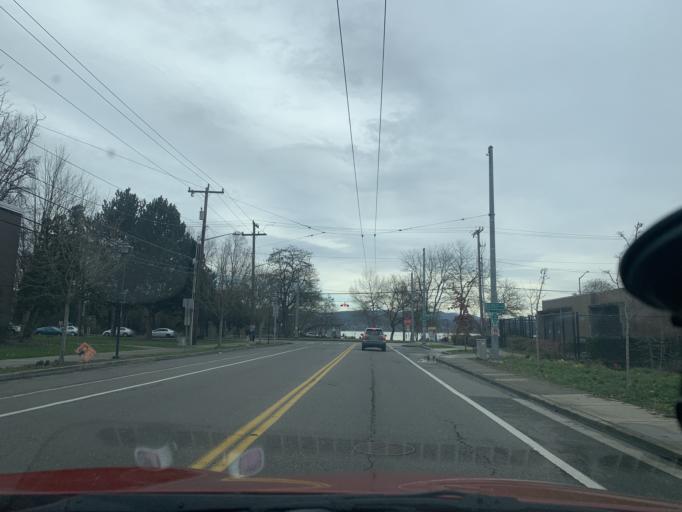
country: US
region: Washington
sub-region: King County
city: Bryn Mawr-Skyway
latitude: 47.5233
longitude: -122.2656
